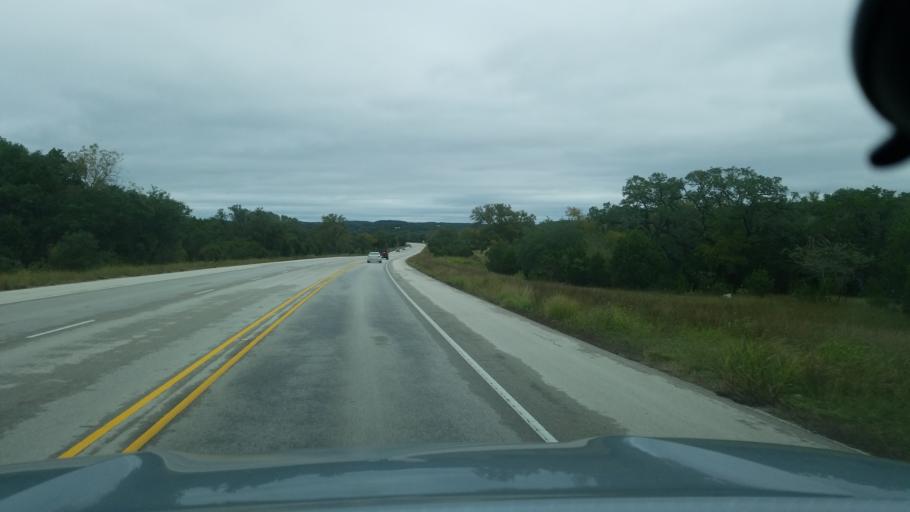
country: US
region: Texas
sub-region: Blanco County
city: Blanco
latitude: 29.9896
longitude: -98.4073
